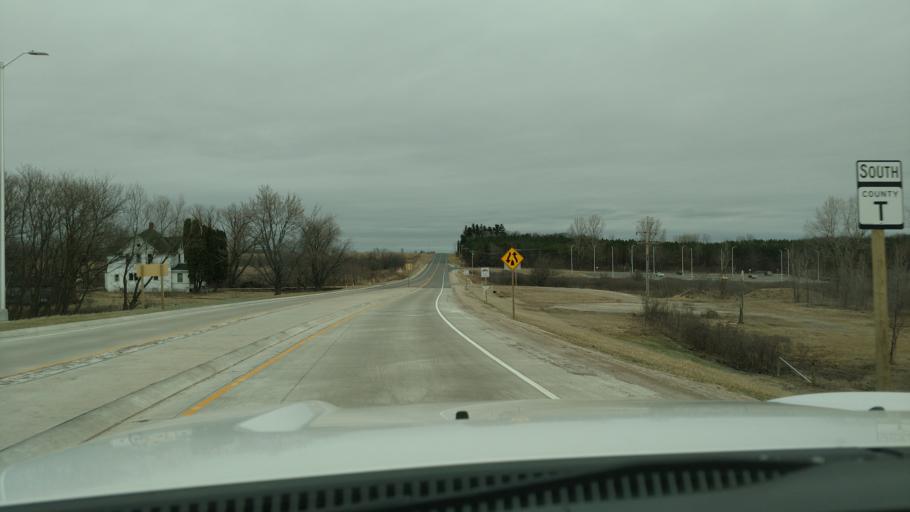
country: US
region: Wisconsin
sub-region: Saint Croix County
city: Hammond
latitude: 44.9411
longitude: -92.4358
